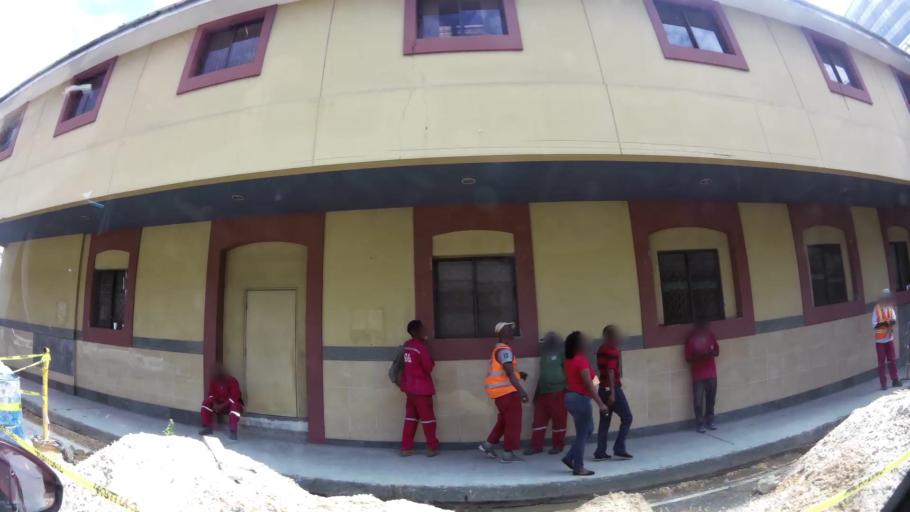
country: TT
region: San Juan/Laventille
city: Laventille
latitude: 10.6515
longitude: -61.5129
